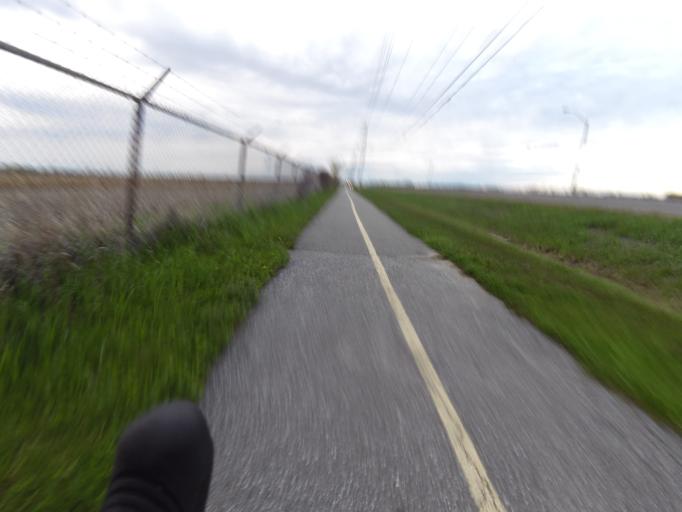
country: CA
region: Ontario
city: Bells Corners
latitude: 45.2940
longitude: -75.7607
